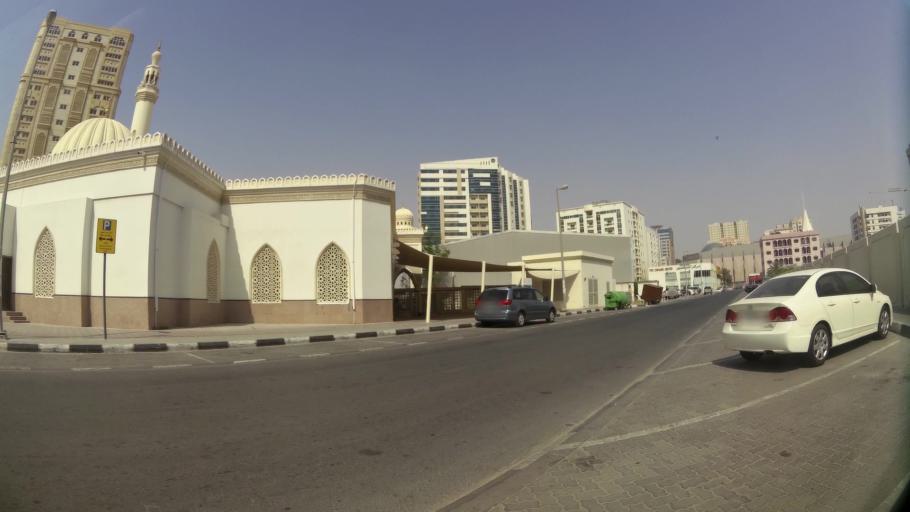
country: AE
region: Ash Shariqah
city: Sharjah
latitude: 25.3470
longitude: 55.3958
